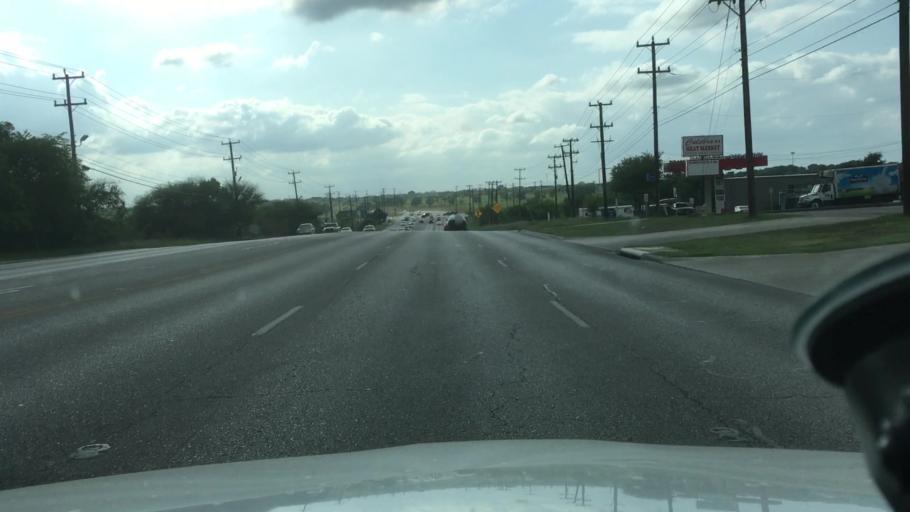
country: US
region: Texas
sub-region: Bexar County
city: Windcrest
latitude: 29.5025
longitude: -98.3631
